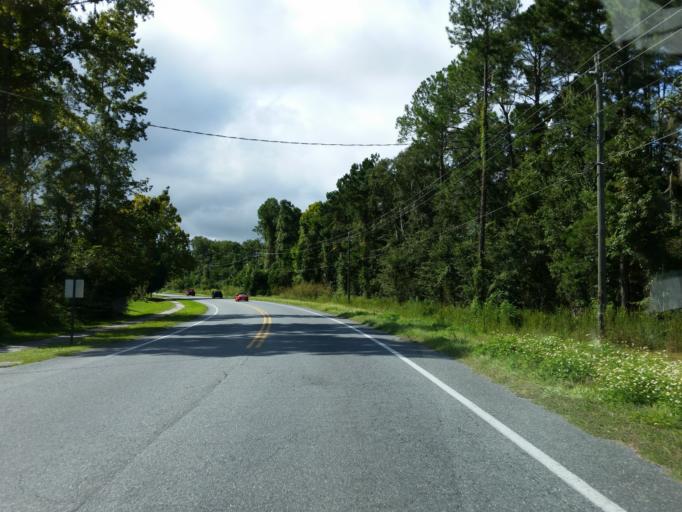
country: US
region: Florida
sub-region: Columbia County
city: Five Points
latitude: 30.2030
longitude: -82.6295
